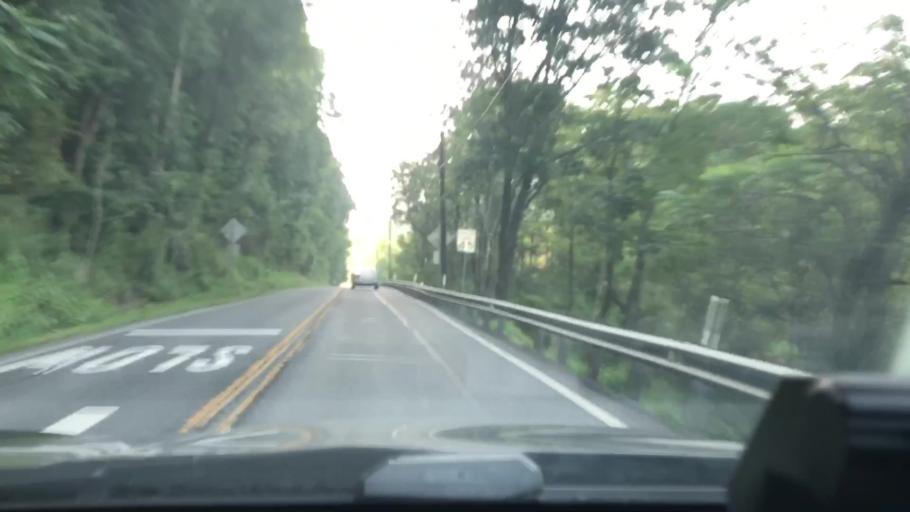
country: US
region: Pennsylvania
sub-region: Berks County
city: Kutztown
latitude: 40.5502
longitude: -75.8007
